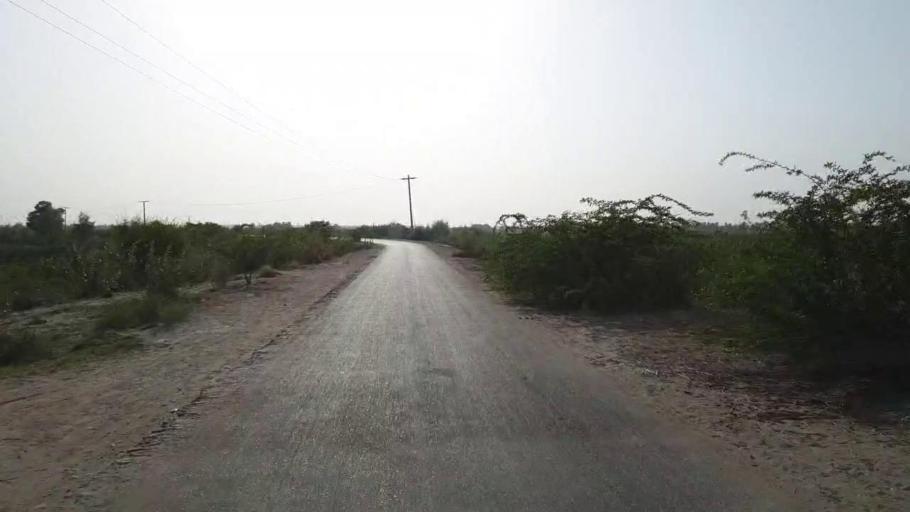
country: PK
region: Sindh
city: Jam Sahib
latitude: 26.4384
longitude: 68.8670
